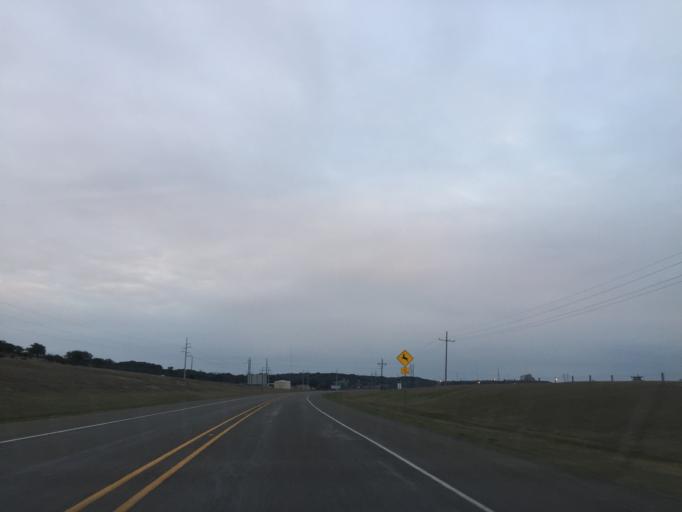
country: US
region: Texas
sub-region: Coryell County
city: Gatesville
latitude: 31.4781
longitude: -97.7249
